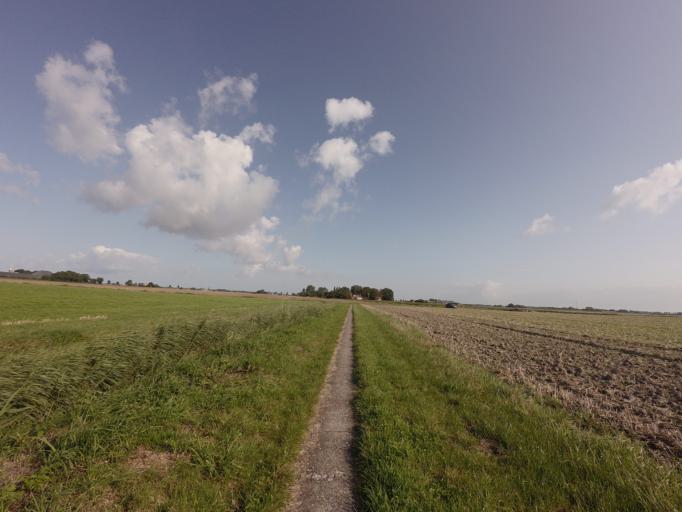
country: NL
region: Friesland
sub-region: Gemeente Franekeradeel
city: Franeker
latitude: 53.2072
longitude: 5.5648
